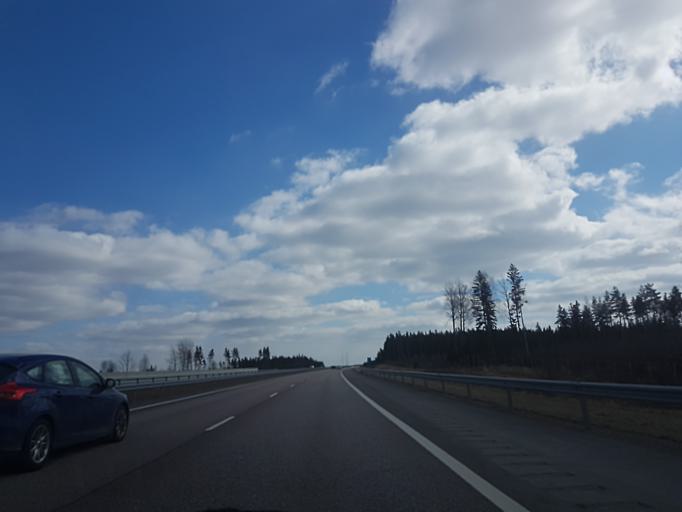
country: FI
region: Uusimaa
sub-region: Loviisa
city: Perna
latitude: 60.4717
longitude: 26.1219
